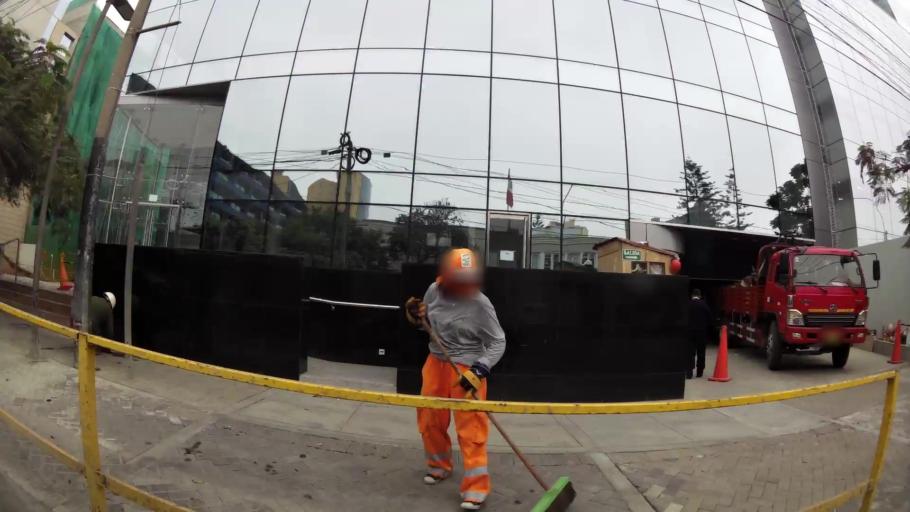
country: PE
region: Lima
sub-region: Lima
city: San Isidro
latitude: -12.0951
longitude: -77.0386
